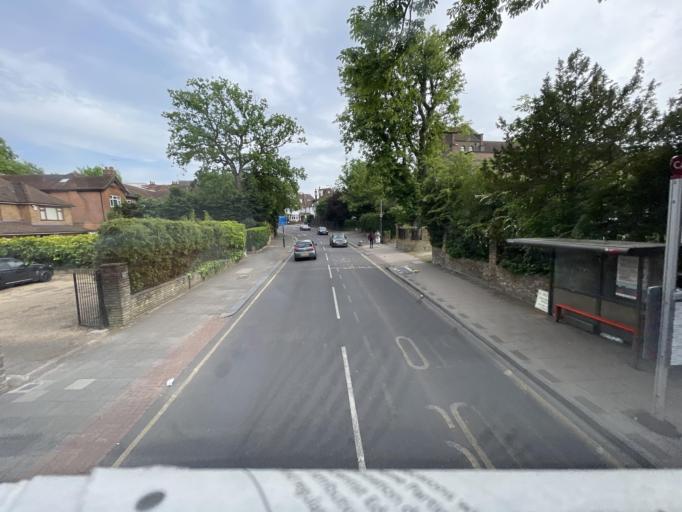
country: GB
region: England
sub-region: Greater London
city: Crouch End
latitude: 51.5942
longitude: -0.1445
